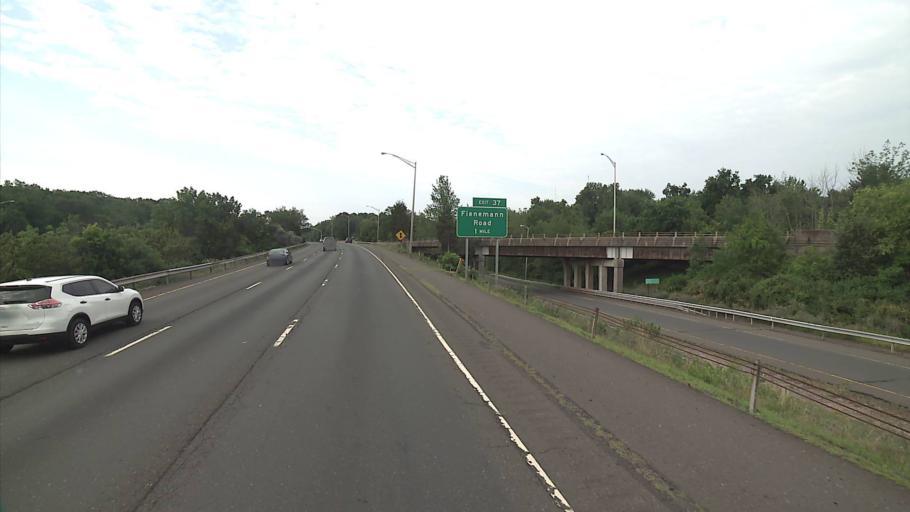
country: US
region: Connecticut
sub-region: Hartford County
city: Farmington
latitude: 41.7201
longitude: -72.7953
